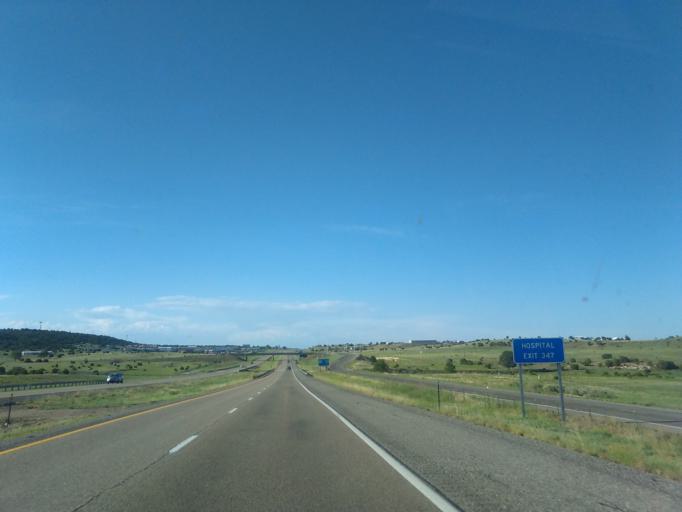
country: US
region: New Mexico
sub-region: San Miguel County
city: Las Vegas
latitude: 35.5514
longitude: -105.2261
